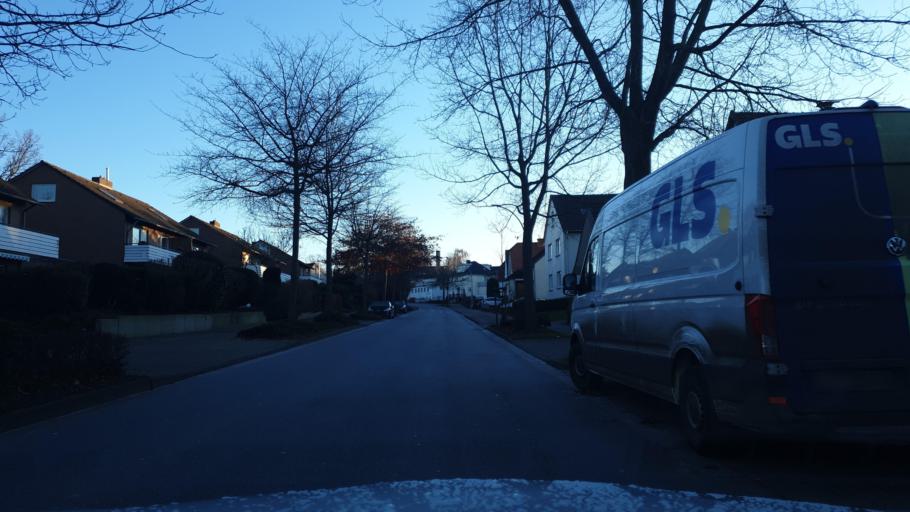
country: DE
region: North Rhine-Westphalia
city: Bad Oeynhausen
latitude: 52.1944
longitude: 8.8170
